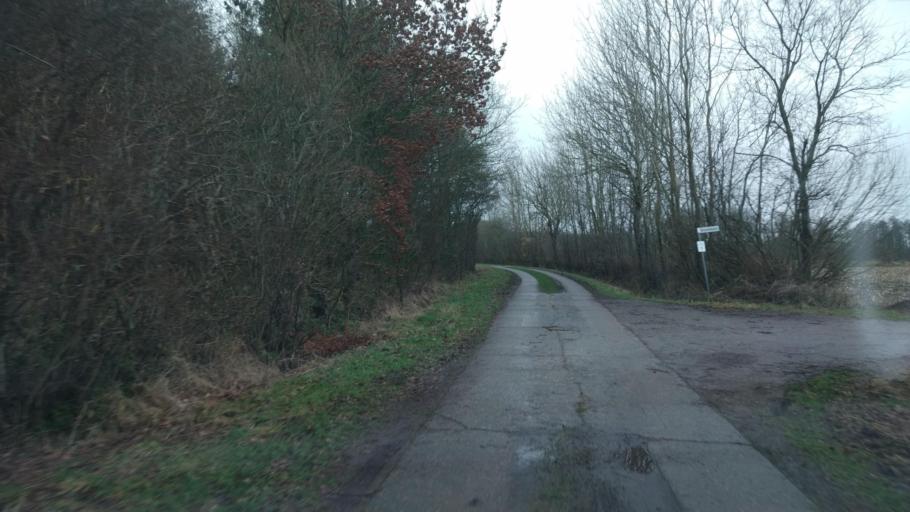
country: DE
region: Schleswig-Holstein
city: Gross Rheide
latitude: 54.4633
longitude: 9.4288
